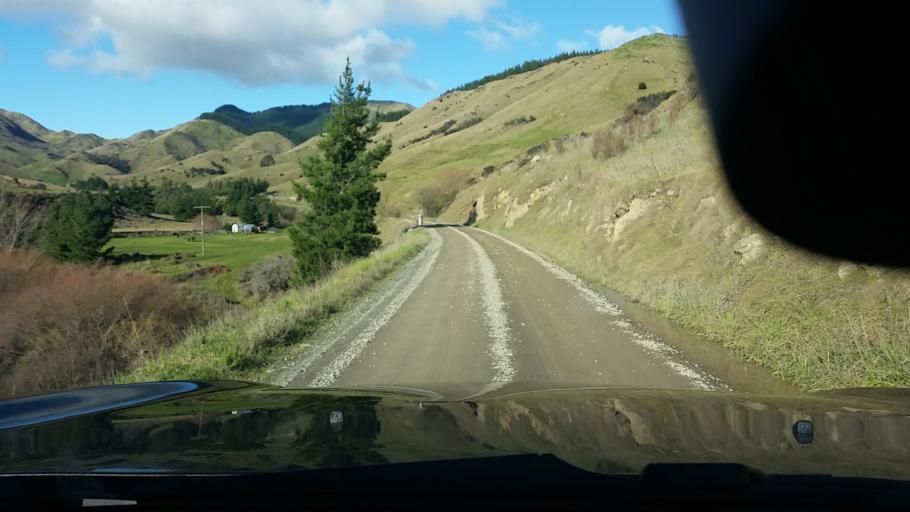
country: NZ
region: Marlborough
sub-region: Marlborough District
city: Blenheim
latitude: -41.6023
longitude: 173.9561
